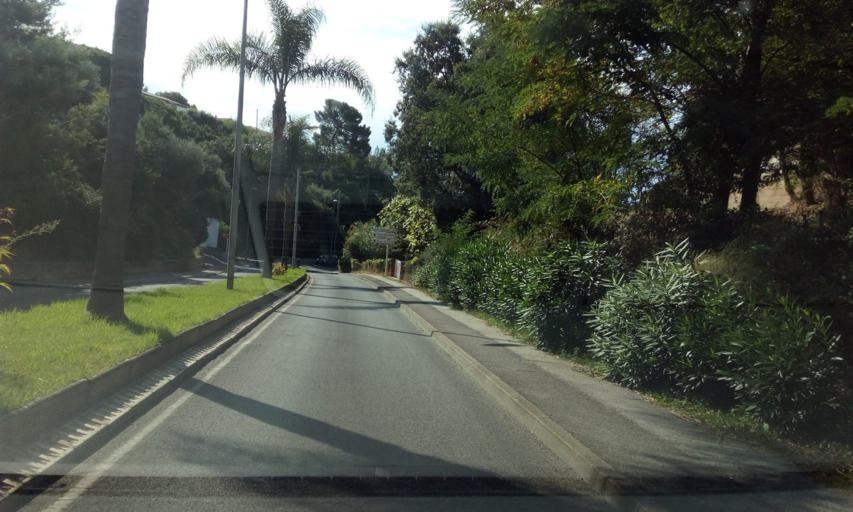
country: FR
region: Provence-Alpes-Cote d'Azur
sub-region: Departement du Var
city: Le Pradet
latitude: 43.1009
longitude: 6.0232
